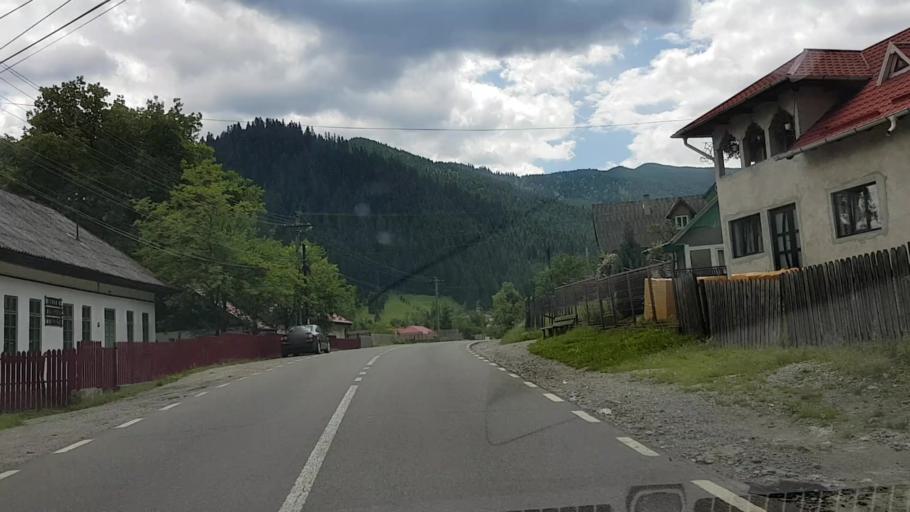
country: RO
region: Neamt
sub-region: Comuna Borca
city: Borca
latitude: 47.2059
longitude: 25.7518
